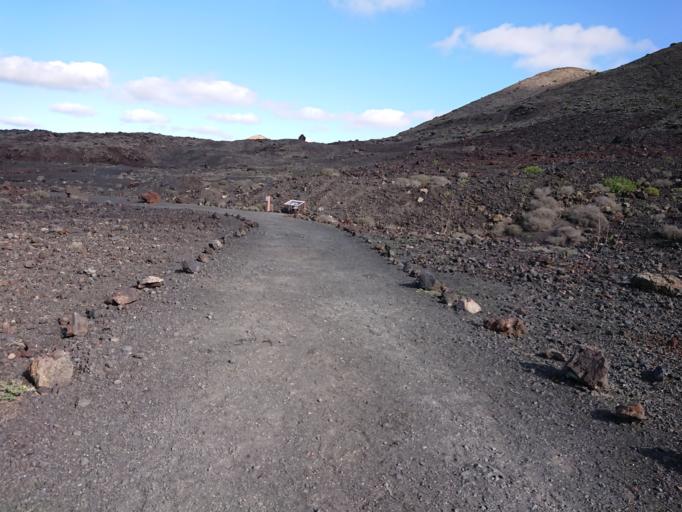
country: ES
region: Canary Islands
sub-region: Provincia de Las Palmas
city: Tias
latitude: 29.0044
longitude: -13.6832
